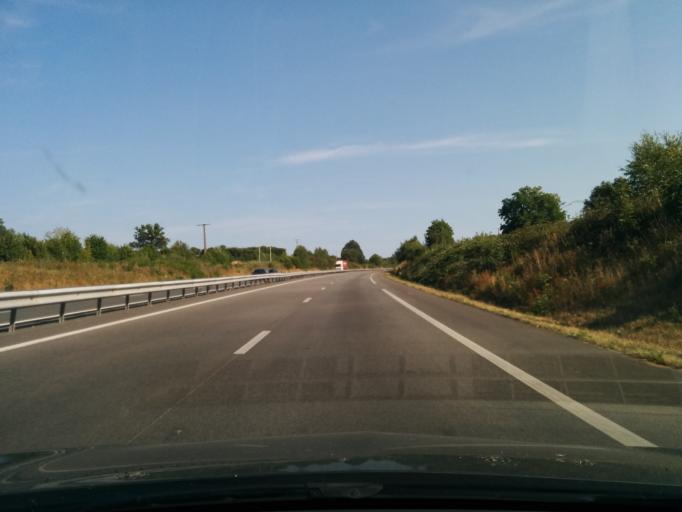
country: FR
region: Limousin
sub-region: Departement de la Haute-Vienne
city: Vicq-sur-Breuilh
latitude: 45.6585
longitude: 1.3992
